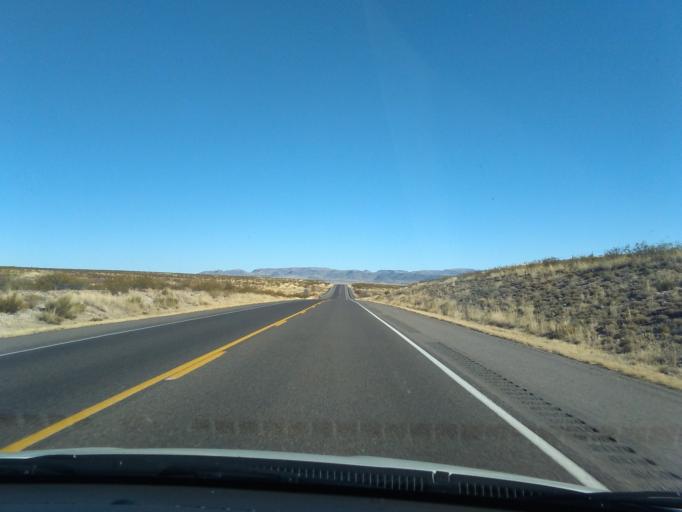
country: US
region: New Mexico
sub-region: Dona Ana County
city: Hatch
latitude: 32.5748
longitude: -107.4179
